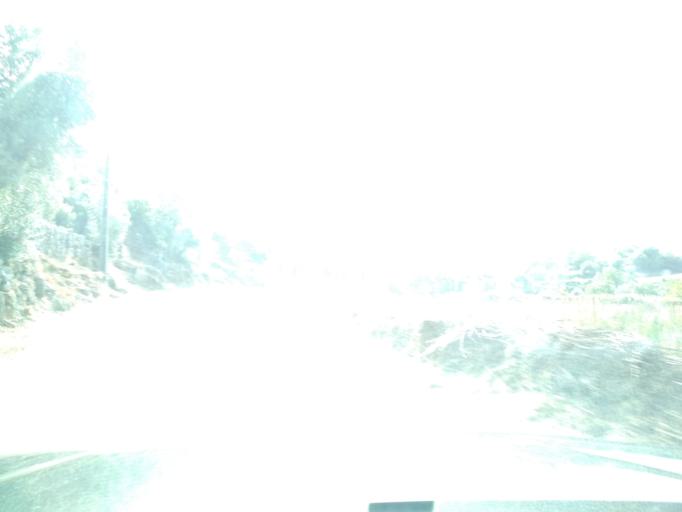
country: PT
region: Coimbra
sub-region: Condeixa-A-Nova
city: Condeixa-a-Nova
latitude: 40.0713
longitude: -8.4998
